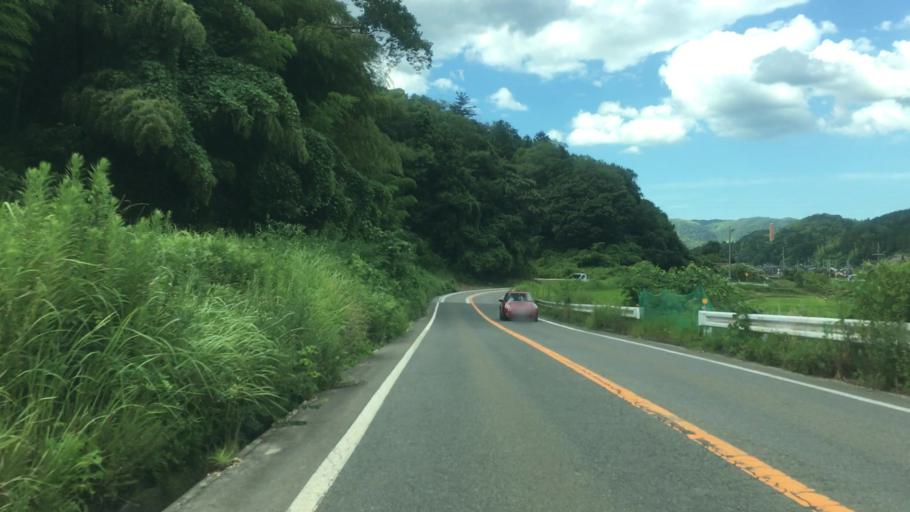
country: JP
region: Hyogo
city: Toyooka
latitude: 35.5335
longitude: 134.7885
